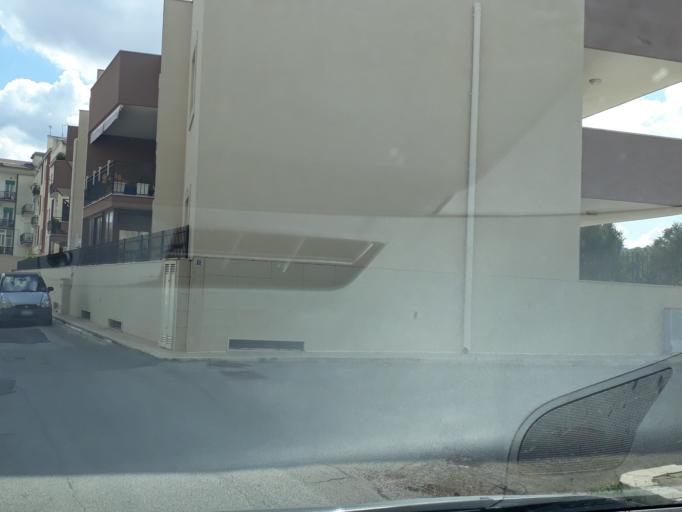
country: IT
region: Apulia
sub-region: Provincia di Brindisi
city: Fasano
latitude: 40.8293
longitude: 17.3545
